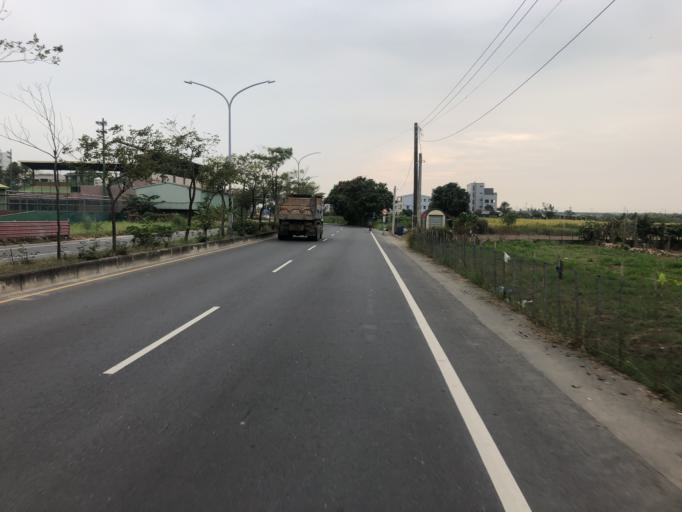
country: TW
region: Taiwan
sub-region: Tainan
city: Tainan
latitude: 23.1377
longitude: 120.2878
